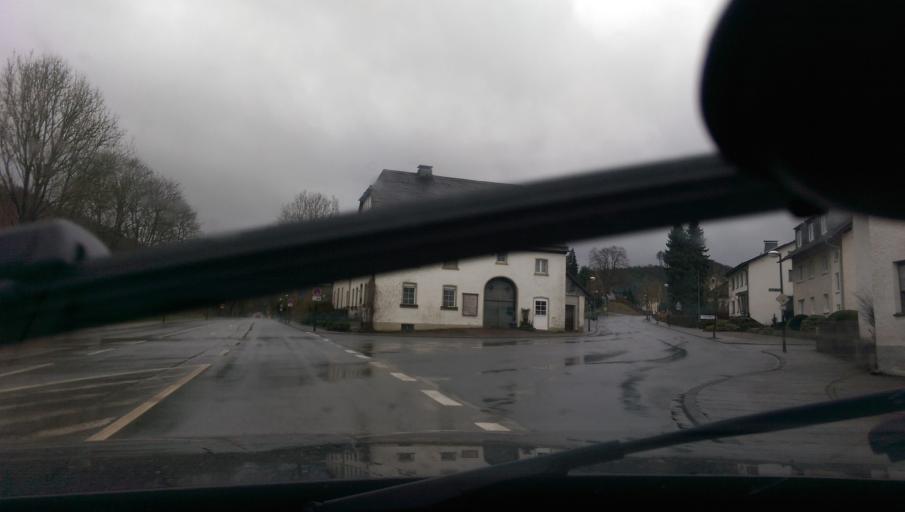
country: DE
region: North Rhine-Westphalia
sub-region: Regierungsbezirk Arnsberg
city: Sundern
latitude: 51.2818
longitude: 7.9504
